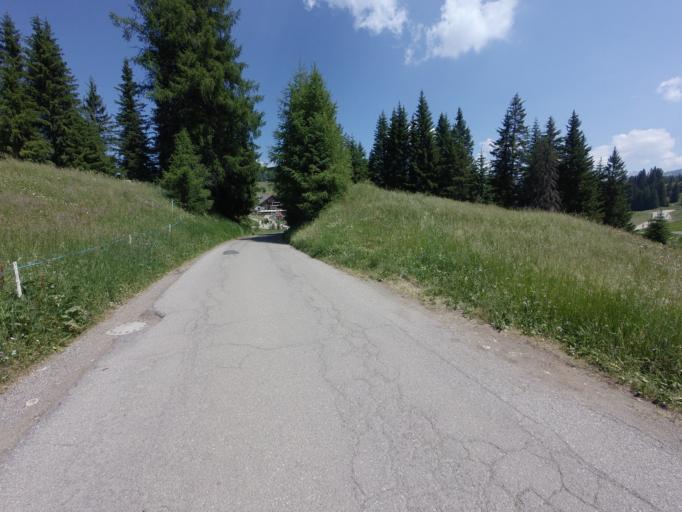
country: IT
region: Trentino-Alto Adige
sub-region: Bolzano
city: Ortisei
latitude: 46.5309
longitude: 11.6681
